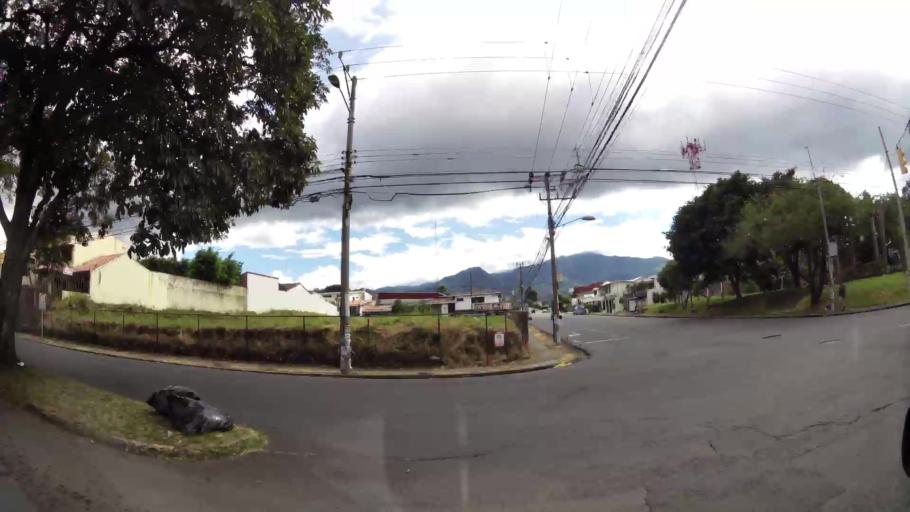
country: CR
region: San Jose
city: San Rafael
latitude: 9.9466
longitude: -84.1228
